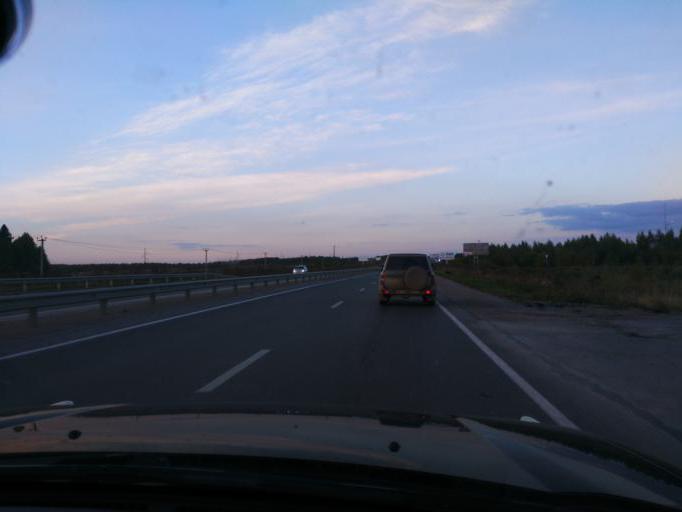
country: RU
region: Perm
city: Polazna
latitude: 58.2061
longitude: 56.4023
